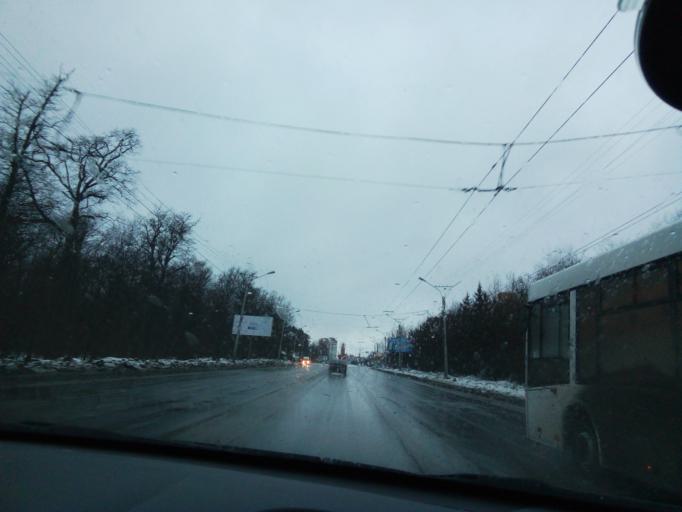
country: RU
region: Chuvashia
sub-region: Cheboksarskiy Rayon
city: Cheboksary
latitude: 56.1359
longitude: 47.1927
